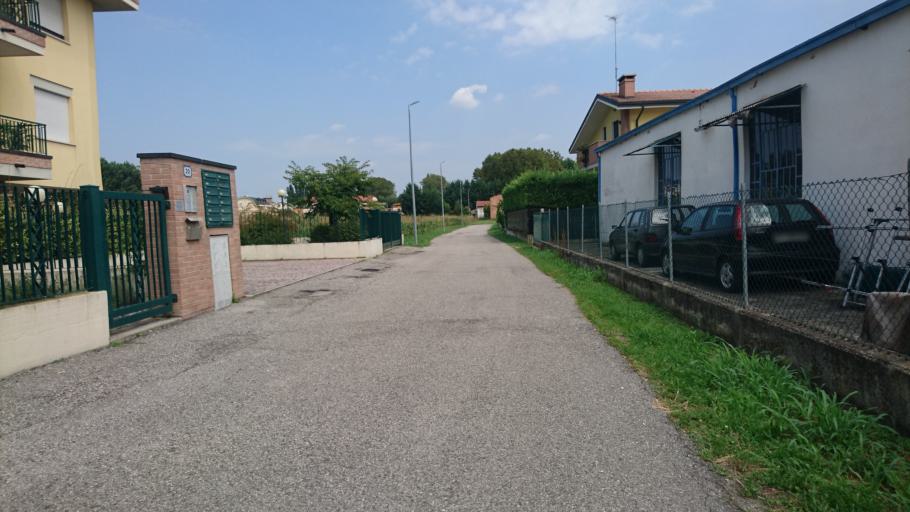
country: IT
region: Veneto
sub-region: Provincia di Padova
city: Padova
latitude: 45.3805
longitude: 11.8829
